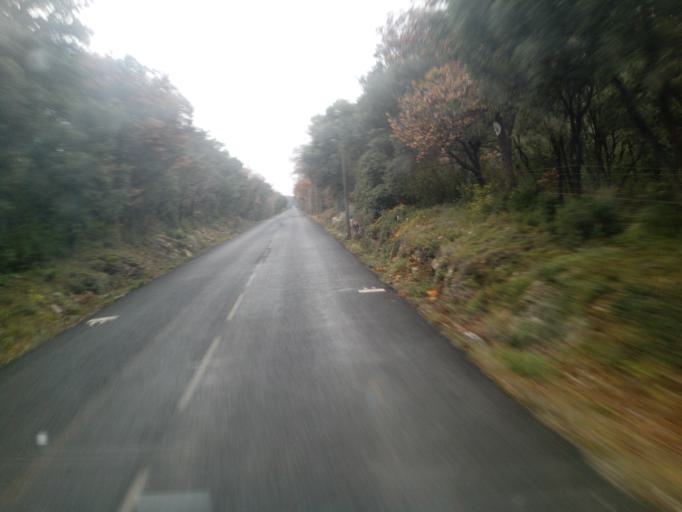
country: FR
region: Languedoc-Roussillon
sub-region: Departement de l'Herault
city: Saint-Martin-de-Londres
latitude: 43.8196
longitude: 3.6697
